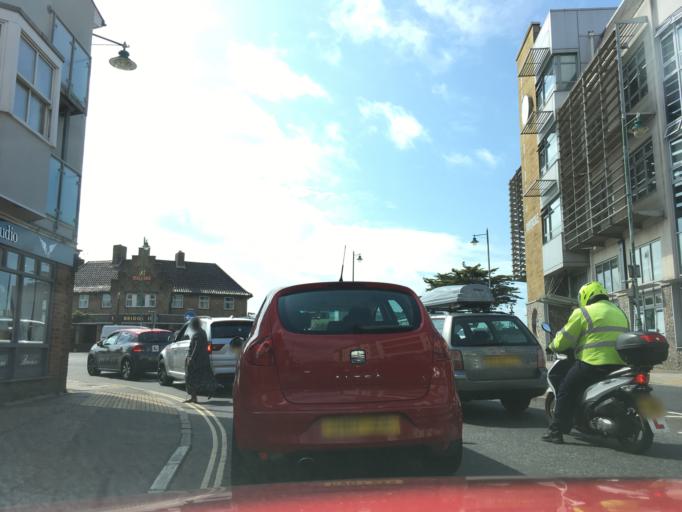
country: GB
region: England
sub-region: West Sussex
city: Shoreham-by-Sea
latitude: 50.8328
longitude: -0.2789
